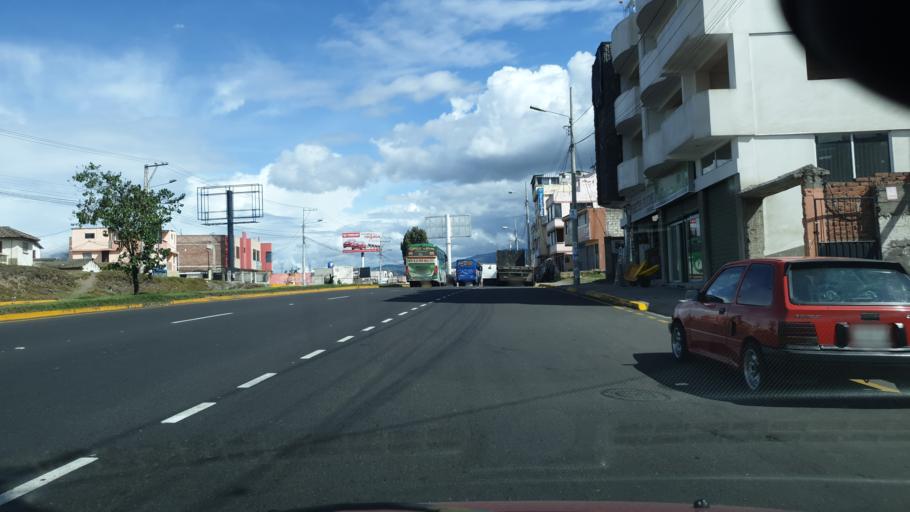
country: EC
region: Tungurahua
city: Ambato
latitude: -1.3039
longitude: -78.6372
